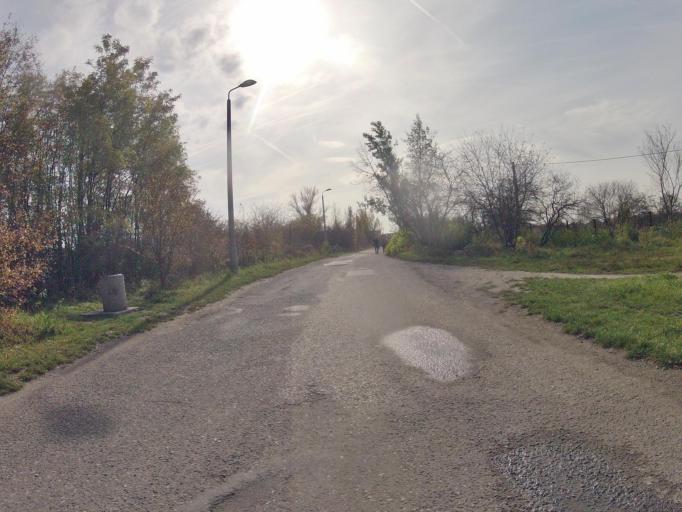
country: PL
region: Lesser Poland Voivodeship
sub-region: Krakow
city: Krakow
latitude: 50.0354
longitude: 19.9134
